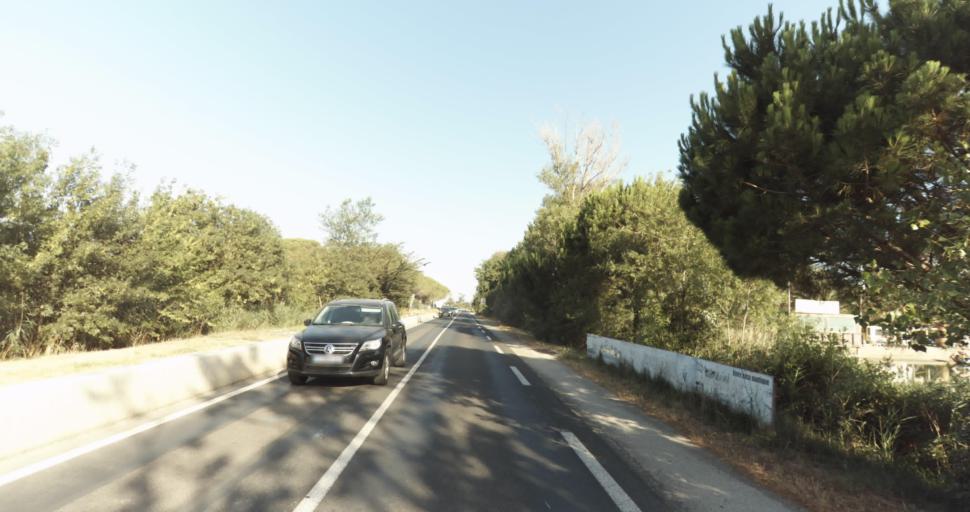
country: FR
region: Languedoc-Roussillon
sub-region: Departement des Pyrenees-Orientales
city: Saint-Cyprien-Plage
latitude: 42.6387
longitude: 3.0211
